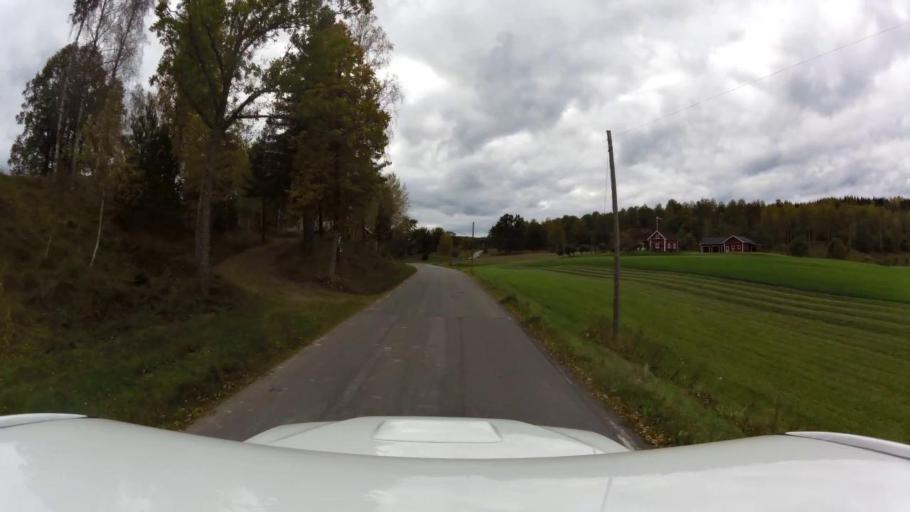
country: SE
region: OEstergoetland
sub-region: Kinda Kommun
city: Rimforsa
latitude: 58.1957
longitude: 15.5684
